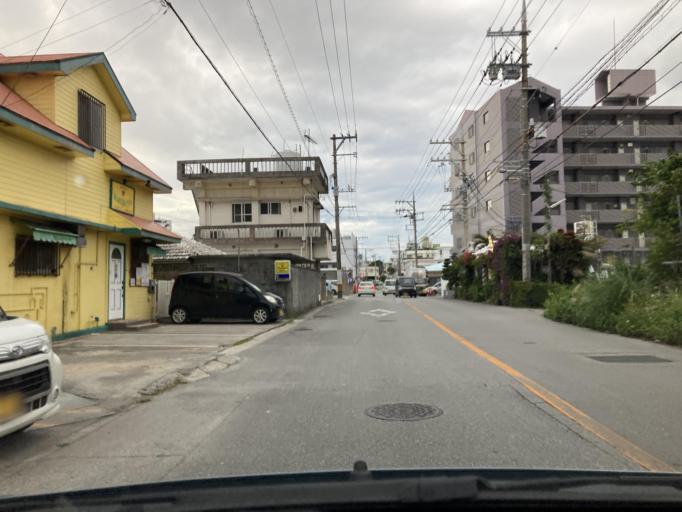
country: JP
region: Okinawa
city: Ginowan
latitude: 26.2691
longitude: 127.7381
